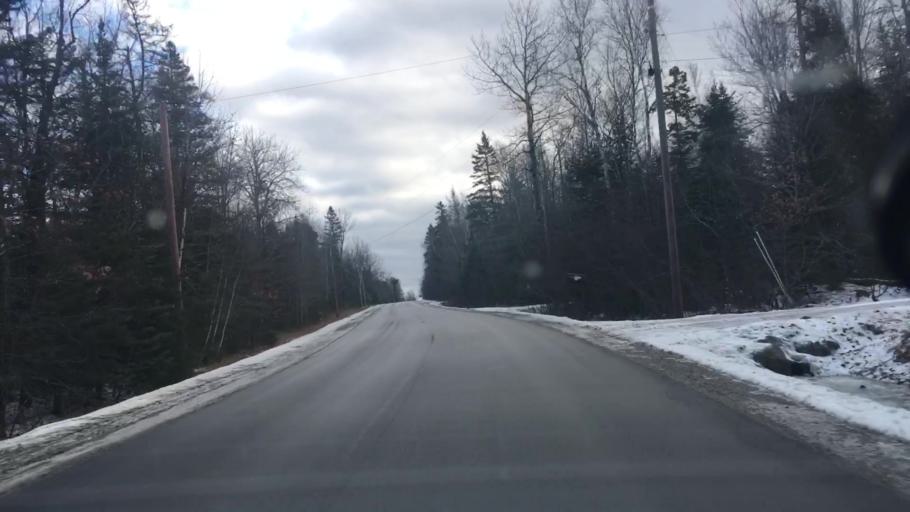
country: US
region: Maine
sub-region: Hancock County
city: Dedham
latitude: 44.6798
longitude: -68.7058
